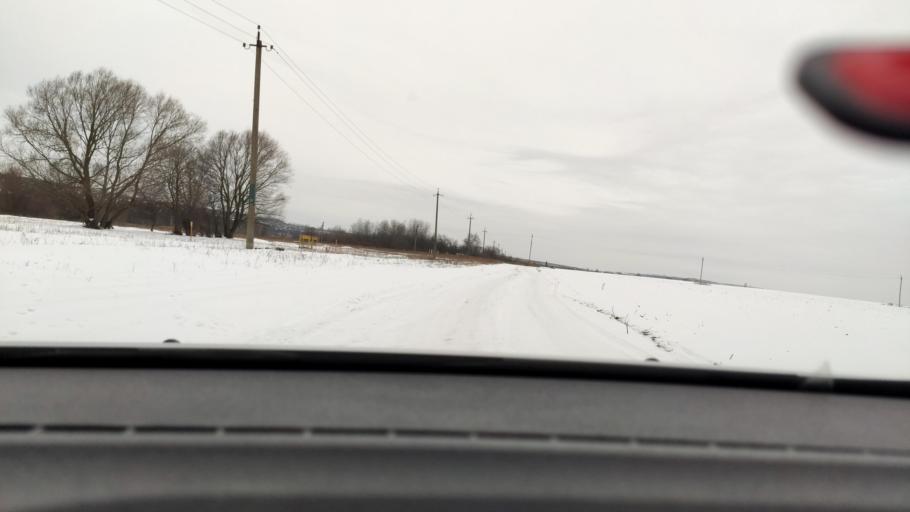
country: RU
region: Voronezj
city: Semiluki
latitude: 51.7022
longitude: 38.9710
